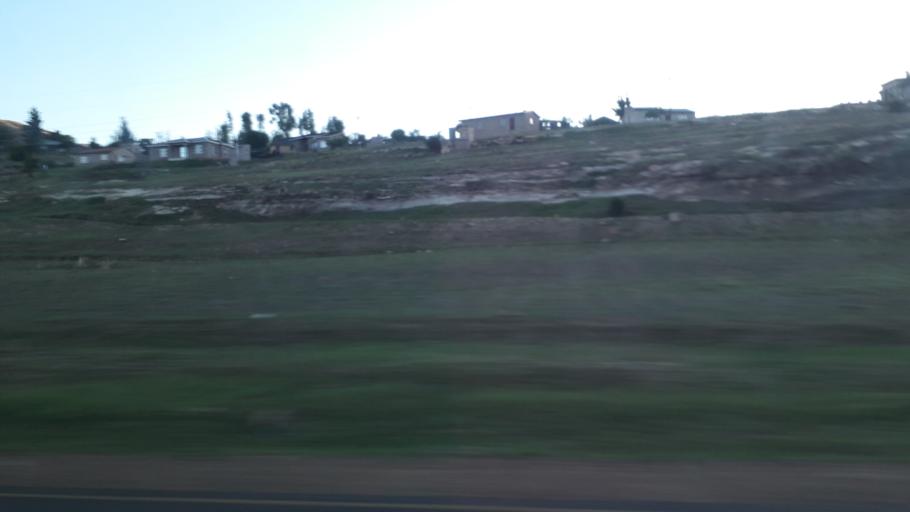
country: LS
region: Butha-Buthe
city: Butha-Buthe
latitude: -28.7294
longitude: 28.3928
